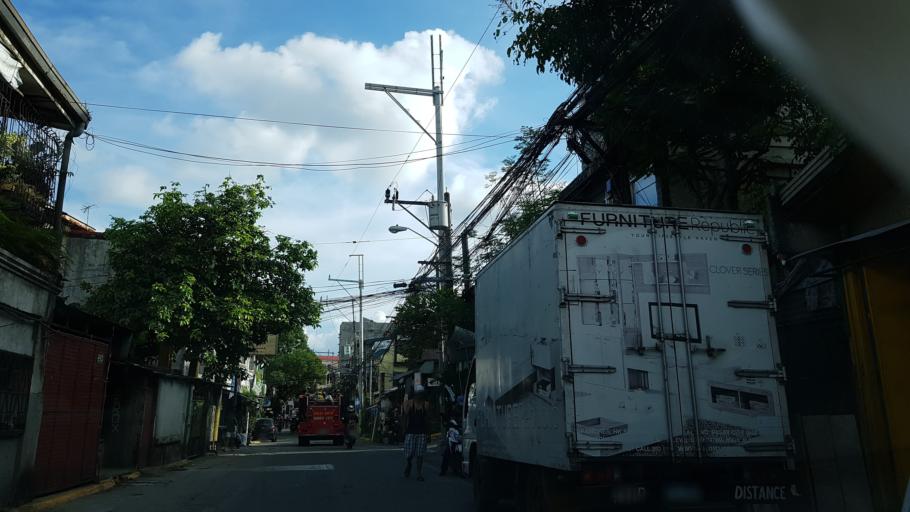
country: PH
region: Calabarzon
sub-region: Province of Rizal
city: Pateros
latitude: 14.5461
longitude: 121.0592
